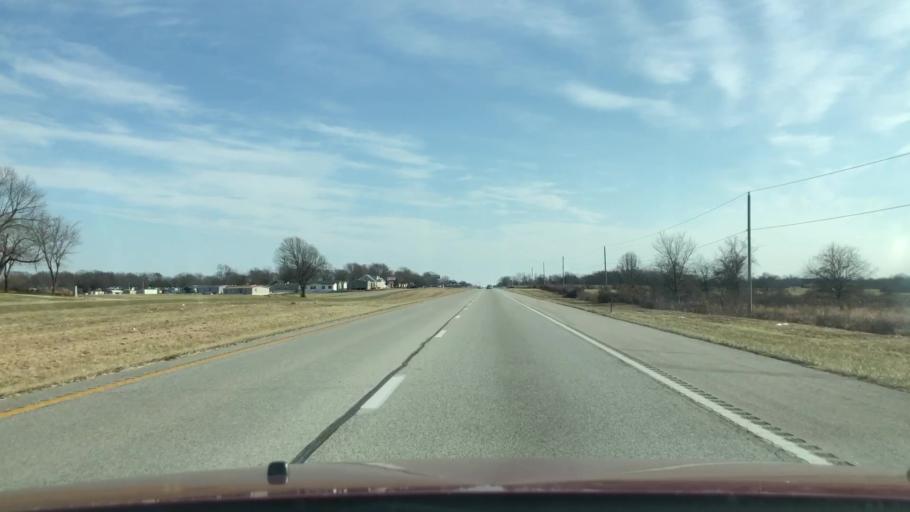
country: US
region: Missouri
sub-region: Webster County
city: Rogersville
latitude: 37.1191
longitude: -93.1369
